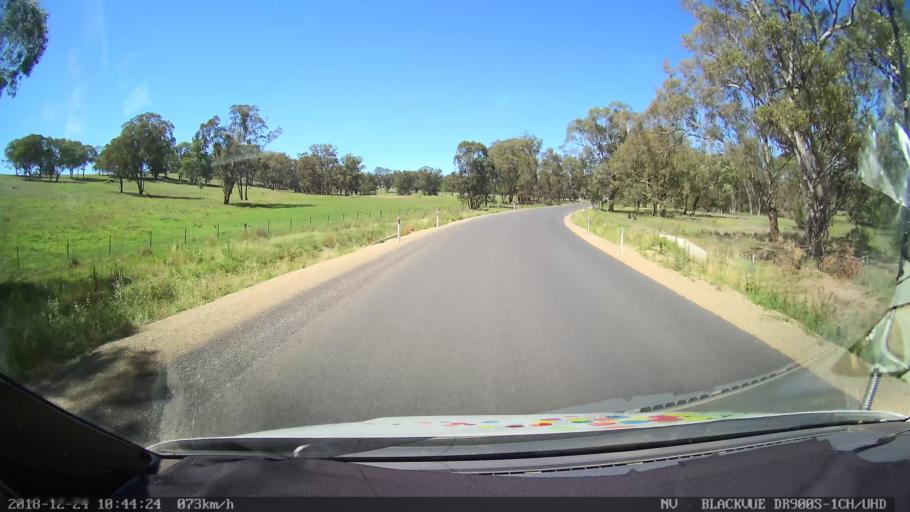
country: AU
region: New South Wales
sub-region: Upper Hunter Shire
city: Merriwa
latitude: -31.8927
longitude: 150.4440
